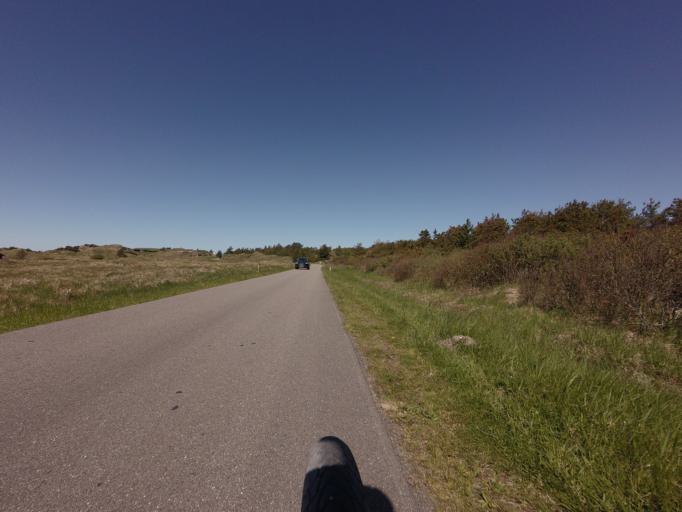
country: DK
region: North Denmark
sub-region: Jammerbugt Kommune
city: Pandrup
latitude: 57.2277
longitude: 9.5660
